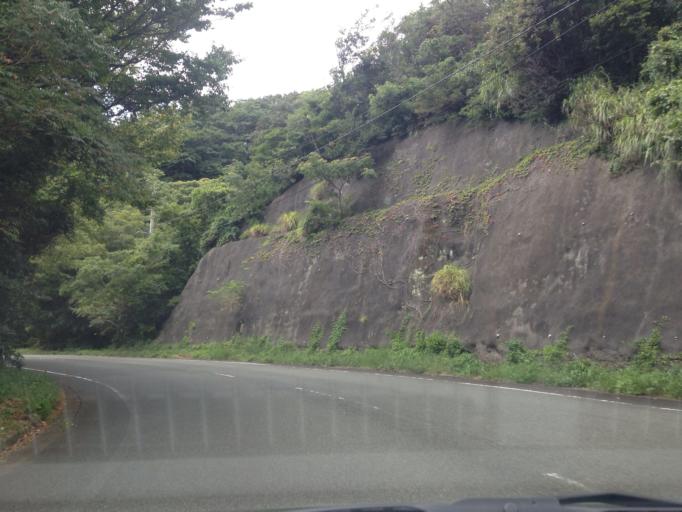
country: JP
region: Shizuoka
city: Shimoda
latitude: 34.6688
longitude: 138.7916
